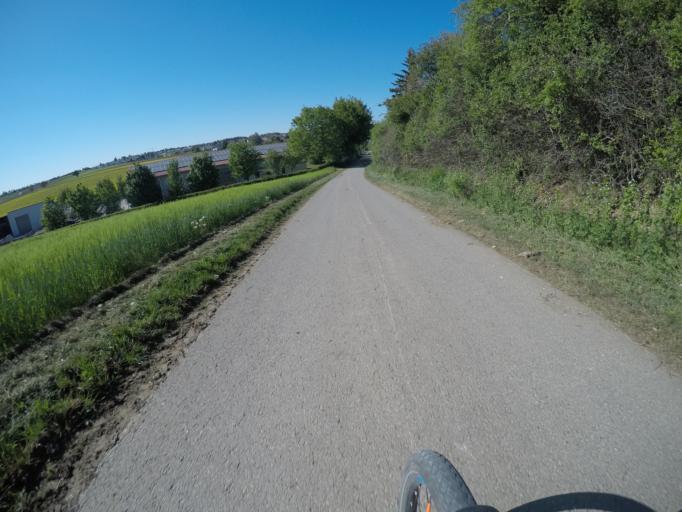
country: DE
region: Baden-Wuerttemberg
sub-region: Karlsruhe Region
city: Friolzheim
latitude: 48.8293
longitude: 8.8414
